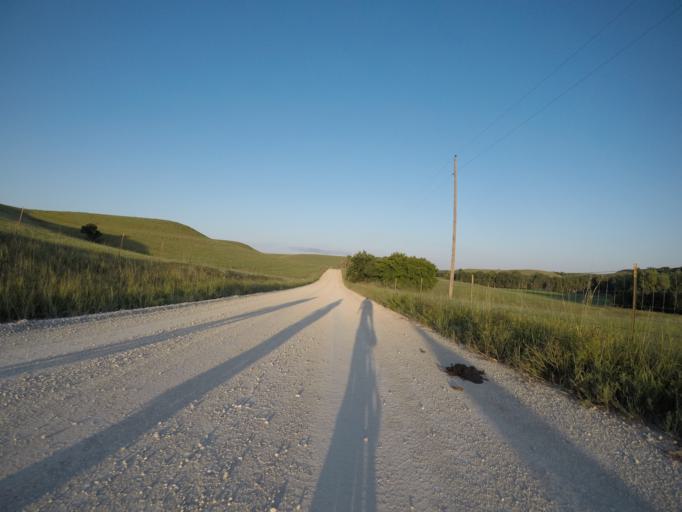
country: US
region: Kansas
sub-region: Riley County
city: Ogden
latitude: 39.0151
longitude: -96.6715
